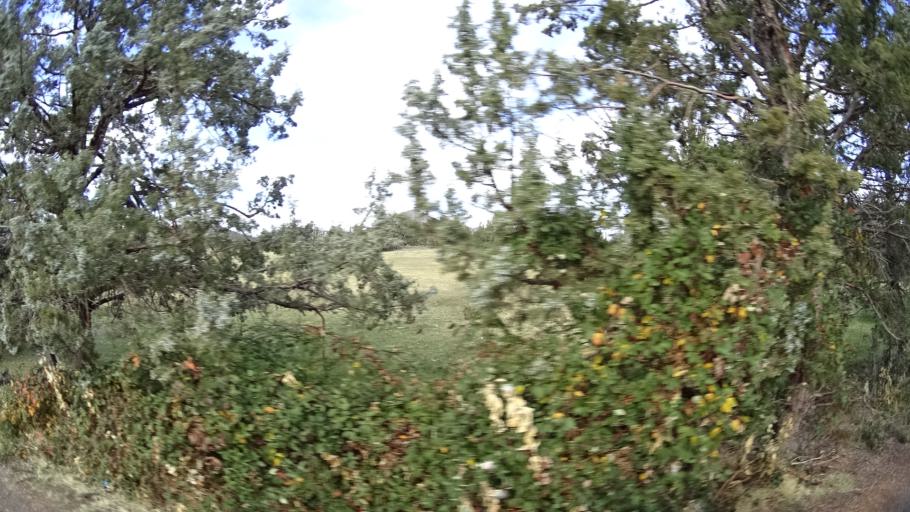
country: US
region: California
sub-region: Siskiyou County
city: Montague
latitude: 41.6385
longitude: -122.4228
